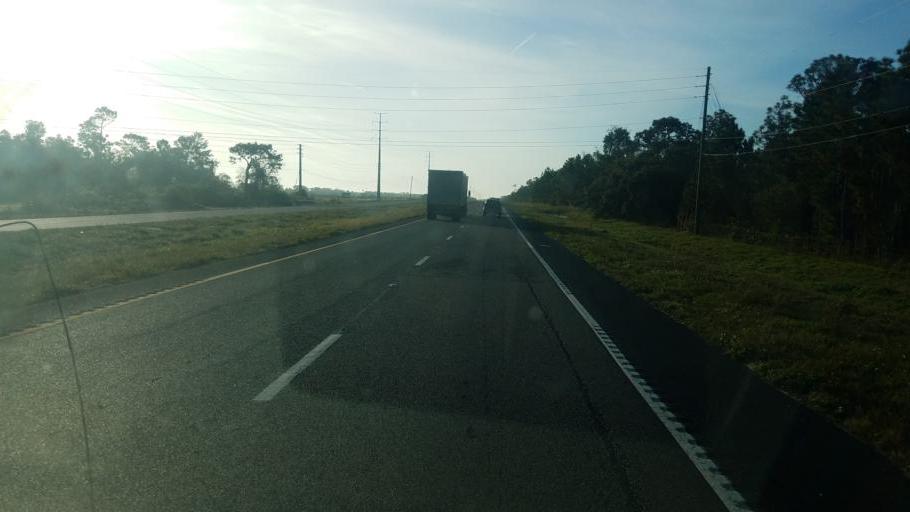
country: US
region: Florida
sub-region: Osceola County
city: Saint Cloud
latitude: 28.2189
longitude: -81.1786
